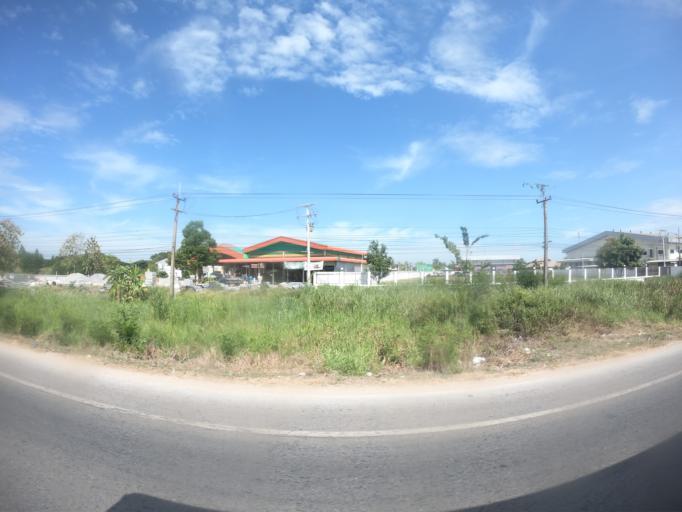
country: TH
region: Khon Kaen
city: Khon Kaen
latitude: 16.4102
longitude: 102.8979
